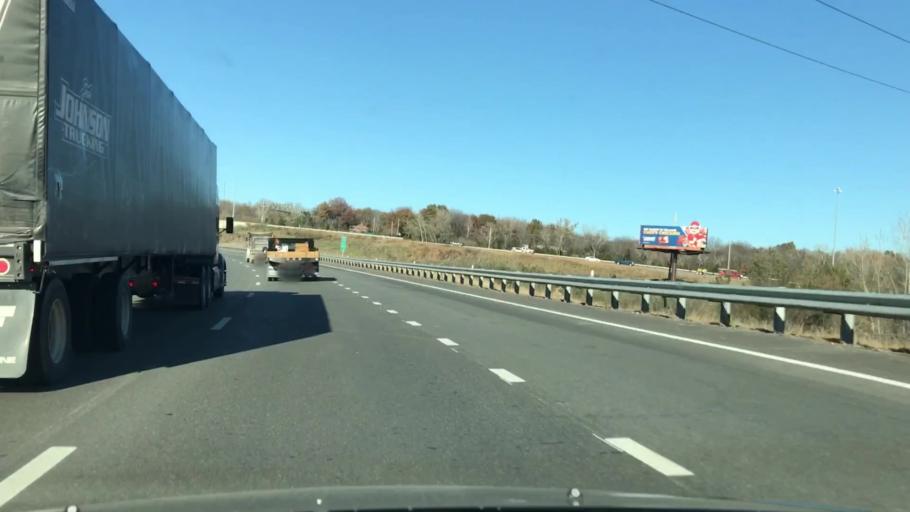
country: US
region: Missouri
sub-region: Jackson County
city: Raytown
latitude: 39.0135
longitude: -94.4971
